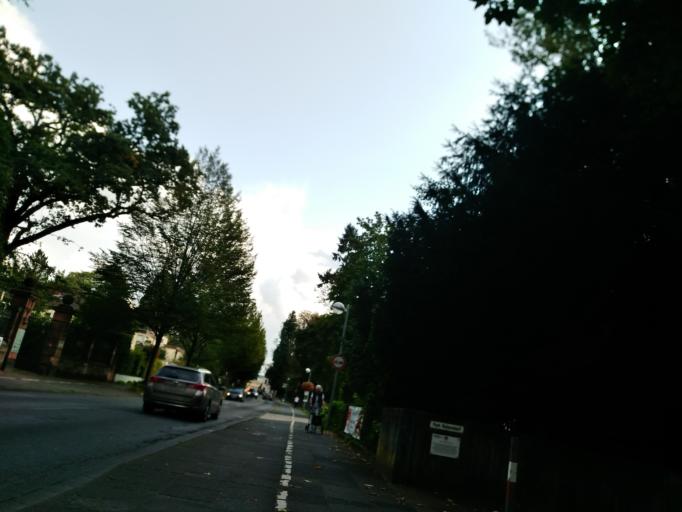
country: DE
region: North Rhine-Westphalia
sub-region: Regierungsbezirk Koln
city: Bad Honnef
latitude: 50.6511
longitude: 7.2192
